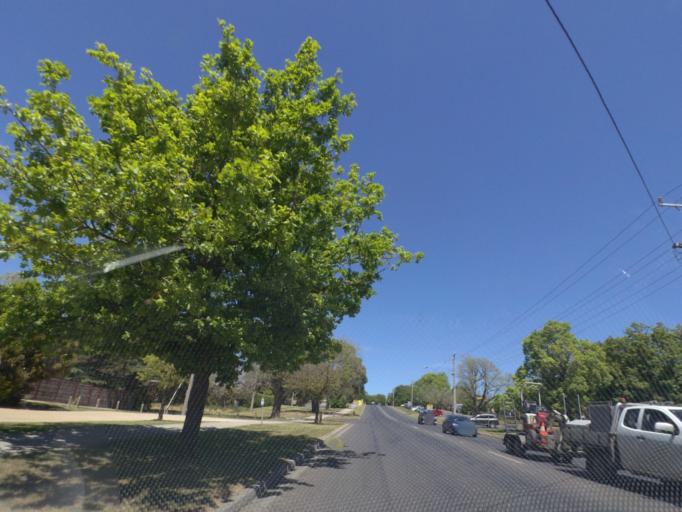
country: AU
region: Victoria
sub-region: Hume
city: Sunbury
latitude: -37.4895
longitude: 144.5909
